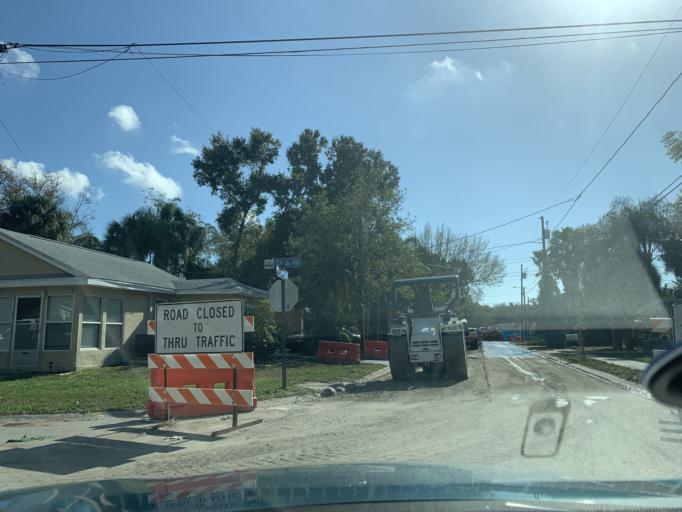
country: US
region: Florida
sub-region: Pinellas County
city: Belleair
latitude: 27.9285
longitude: -82.7993
